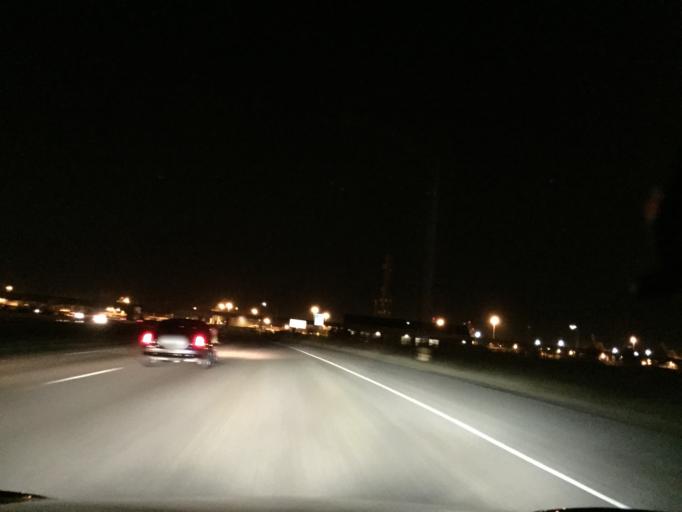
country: US
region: California
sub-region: Alameda County
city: Emeryville
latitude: 37.8101
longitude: -122.3048
